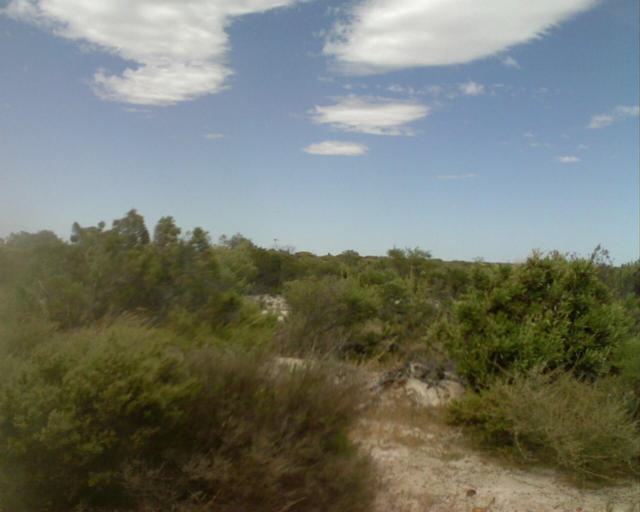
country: AU
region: Western Australia
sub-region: Moora
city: Moora
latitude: -30.0508
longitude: 115.6903
